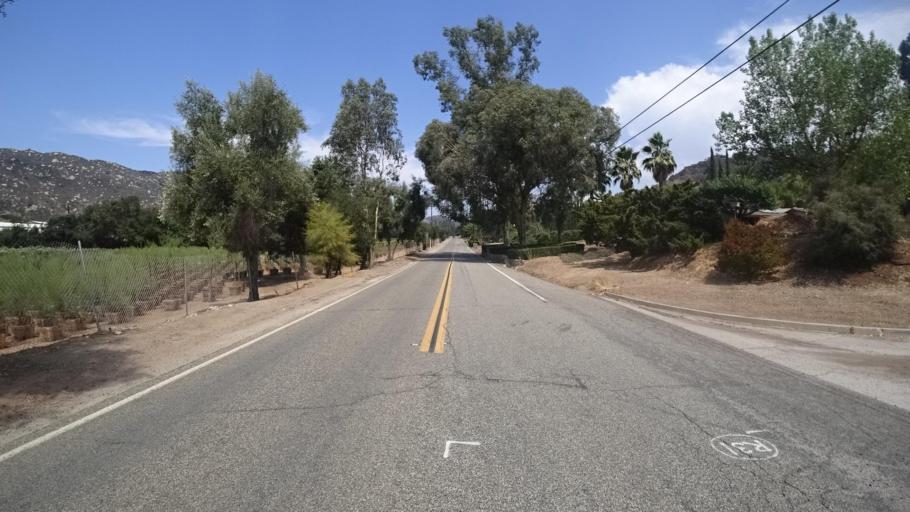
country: US
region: California
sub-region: San Diego County
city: Hidden Meadows
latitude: 33.1879
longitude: -117.0917
